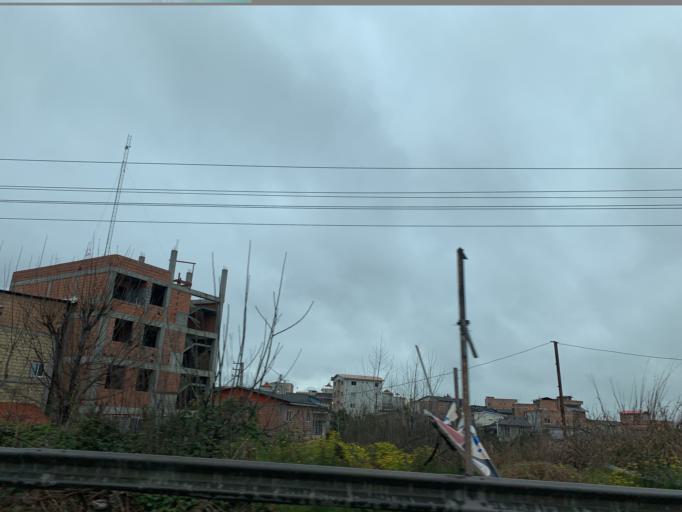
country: IR
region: Mazandaran
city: Amol
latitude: 36.4073
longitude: 52.3480
